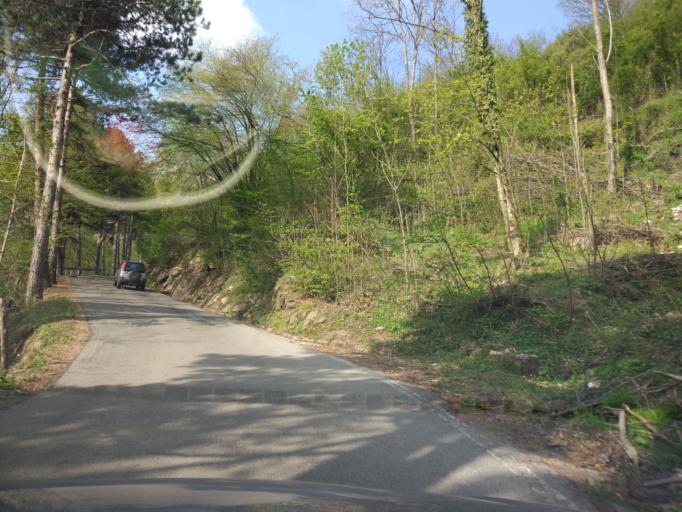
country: IT
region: Lombardy
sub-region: Provincia di Lecco
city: Ballabio
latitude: 45.8969
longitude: 9.4099
